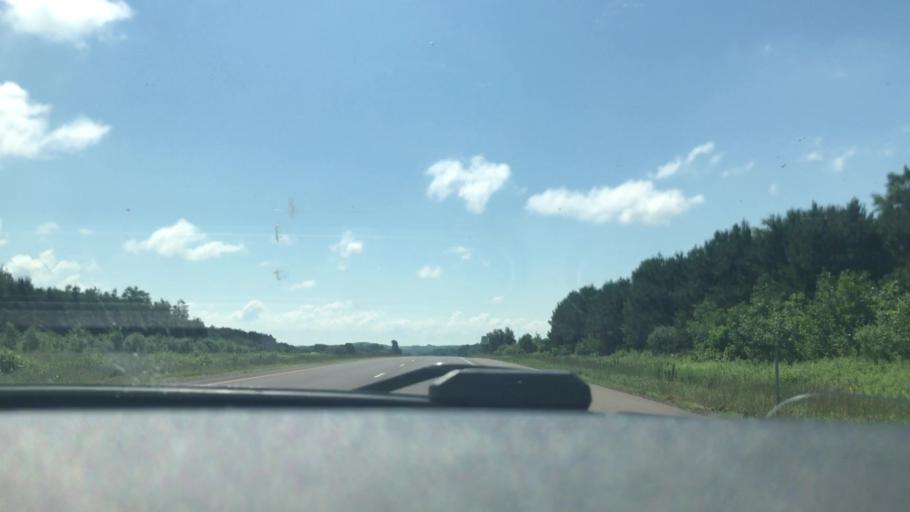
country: US
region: Wisconsin
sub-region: Chippewa County
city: Bloomer
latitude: 45.0865
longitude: -91.4864
